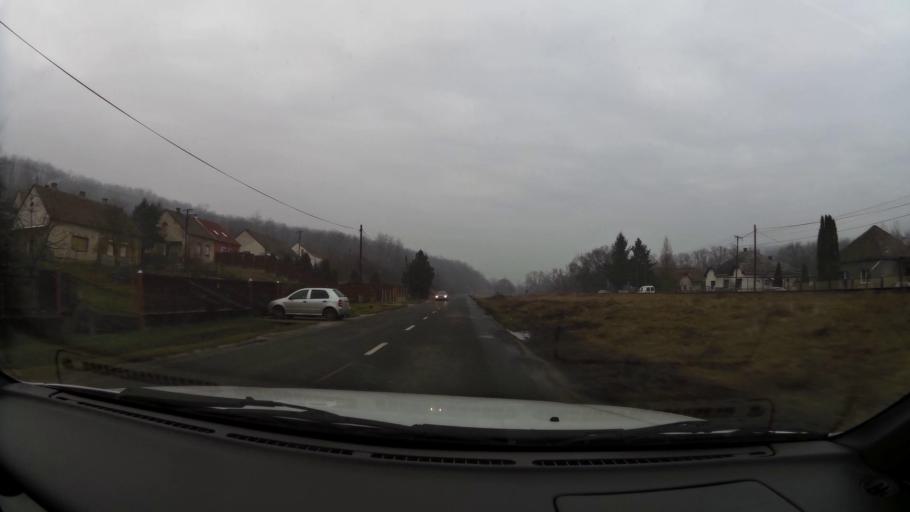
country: HU
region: Borsod-Abauj-Zemplen
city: Rudabanya
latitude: 48.3408
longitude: 20.6455
